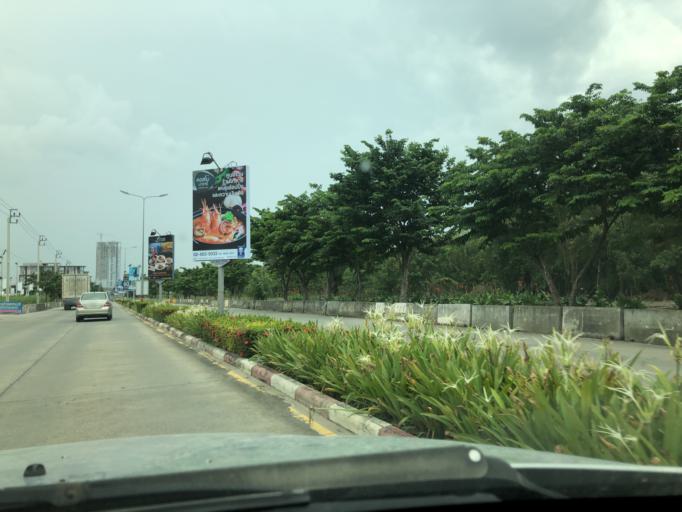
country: TH
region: Nonthaburi
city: Pak Kret
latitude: 13.9283
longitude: 100.5415
